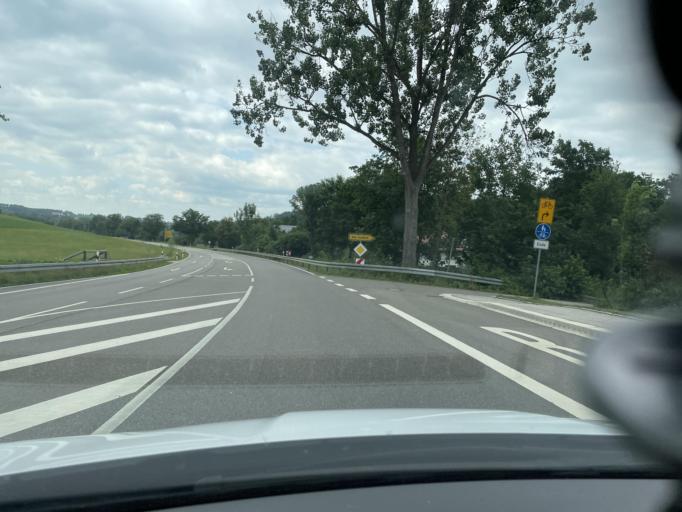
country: DE
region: Bavaria
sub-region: Upper Bavaria
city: Sankt Wolfgang
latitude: 48.2016
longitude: 12.1456
